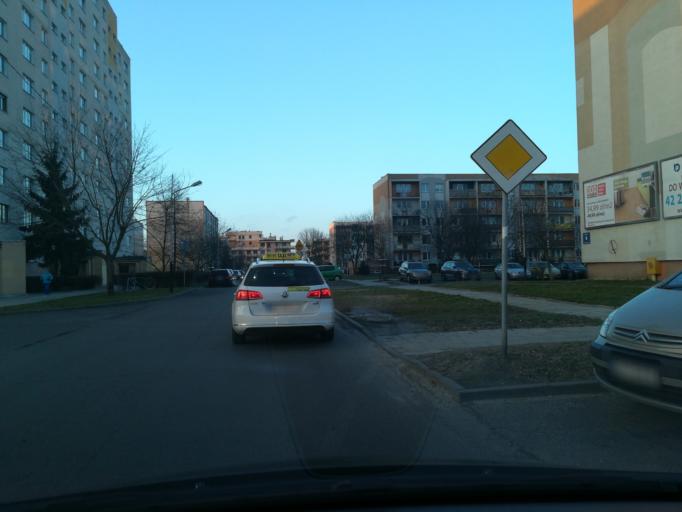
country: PL
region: Lodz Voivodeship
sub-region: Piotrkow Trybunalski
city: Piotrkow Trybunalski
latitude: 51.4110
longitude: 19.6595
